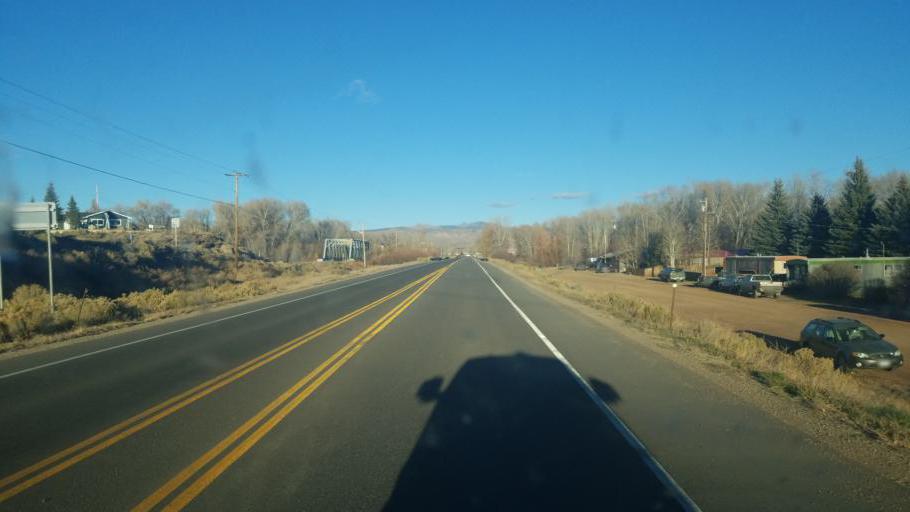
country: US
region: Colorado
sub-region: Gunnison County
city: Gunnison
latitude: 38.5316
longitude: -106.9542
